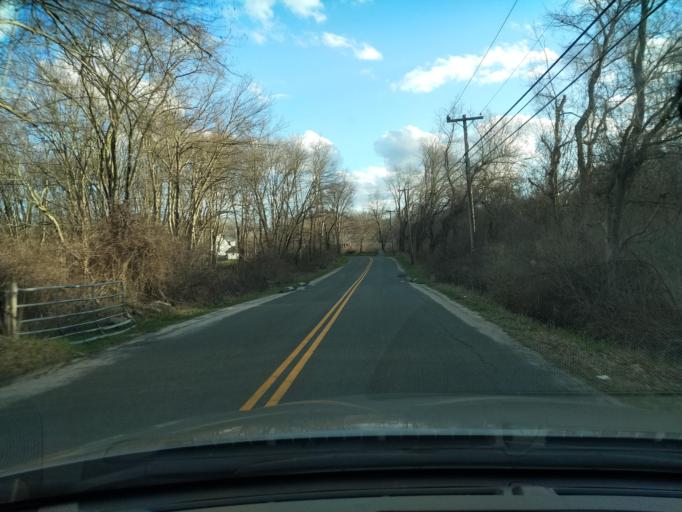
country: US
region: Connecticut
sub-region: Fairfield County
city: Newtown
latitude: 41.3669
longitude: -73.2836
